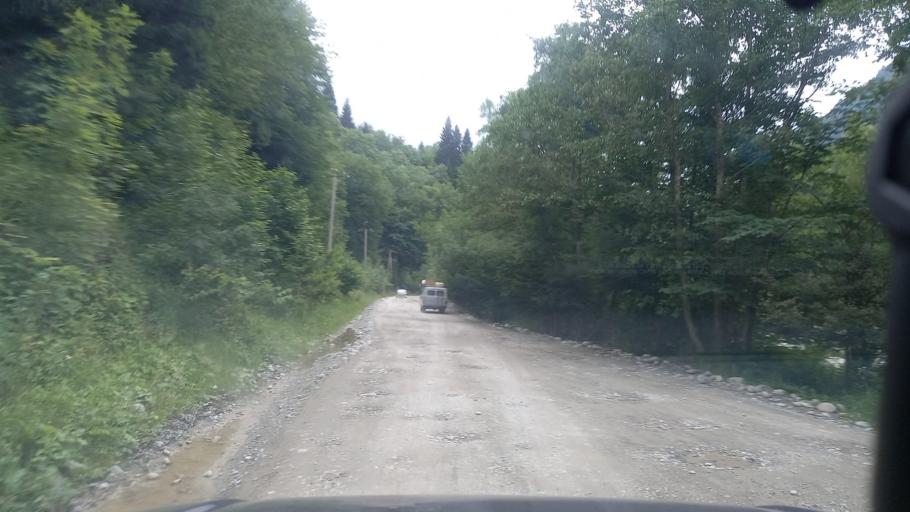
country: RU
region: Karachayevo-Cherkesiya
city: Kurdzhinovo
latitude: 43.8112
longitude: 40.9127
